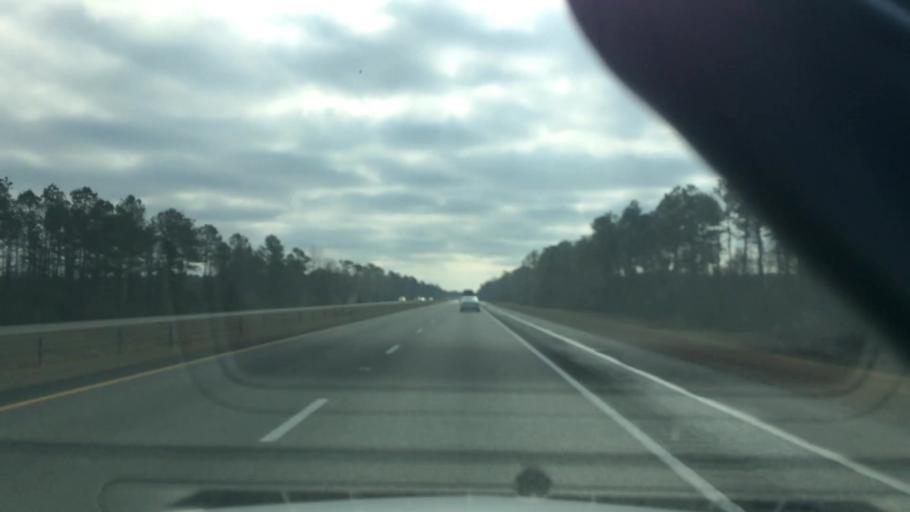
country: US
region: North Carolina
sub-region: Pender County
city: Rocky Point
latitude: 34.4089
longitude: -77.8710
